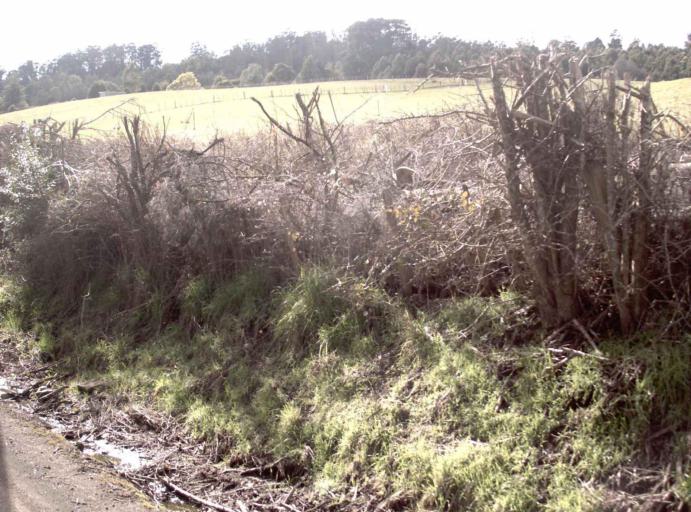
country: AU
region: Tasmania
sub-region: Launceston
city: Mayfield
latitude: -41.2473
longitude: 147.2463
